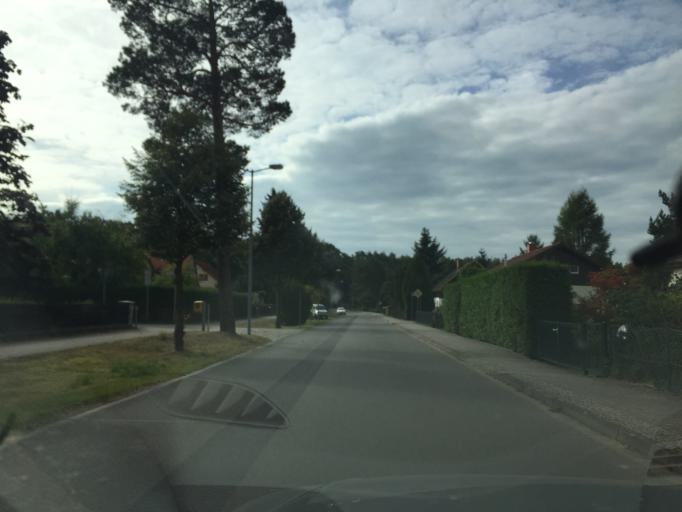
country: DE
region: Brandenburg
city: Erkner
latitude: 52.4083
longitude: 13.7632
